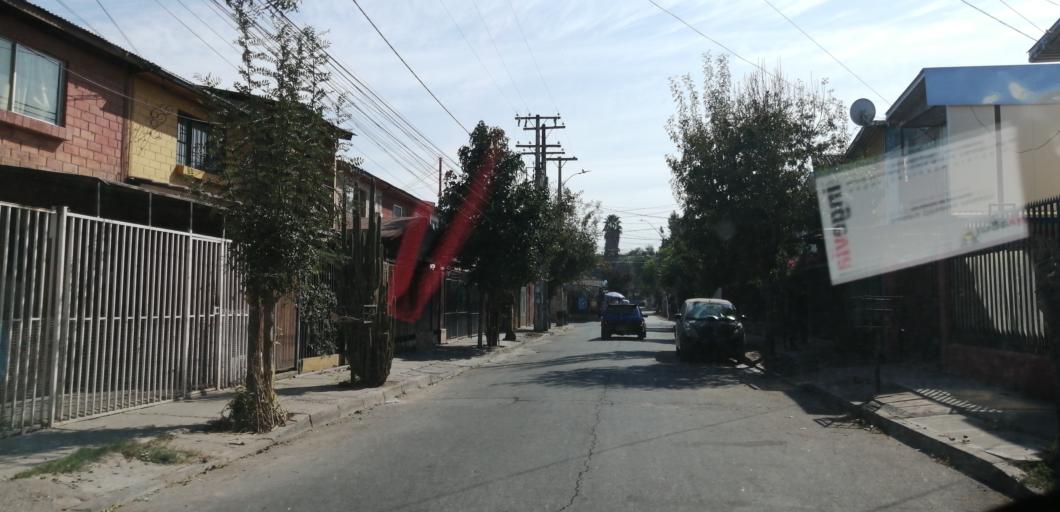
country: CL
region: Santiago Metropolitan
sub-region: Provincia de Santiago
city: Lo Prado
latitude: -33.4586
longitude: -70.7480
